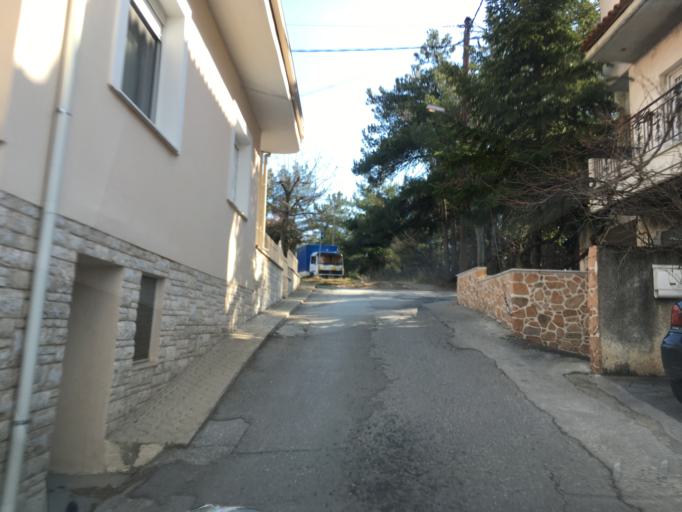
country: GR
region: West Macedonia
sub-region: Nomos Kozanis
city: Kozani
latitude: 40.3042
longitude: 21.7813
